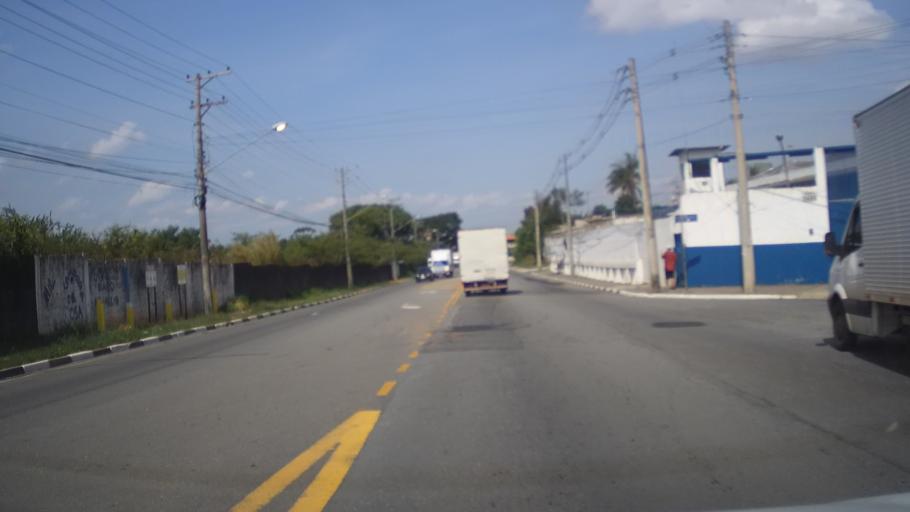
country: BR
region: Sao Paulo
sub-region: Guarulhos
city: Guarulhos
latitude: -23.4363
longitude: -46.4656
